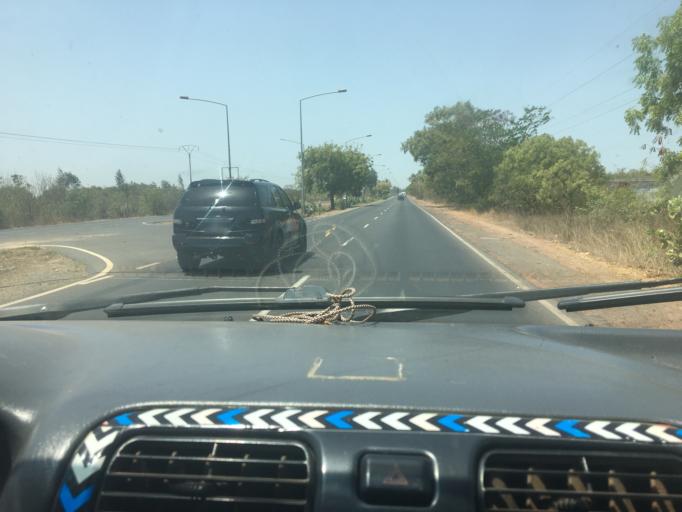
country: GM
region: Banjul
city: Bakau
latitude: 13.4684
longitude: -16.6443
